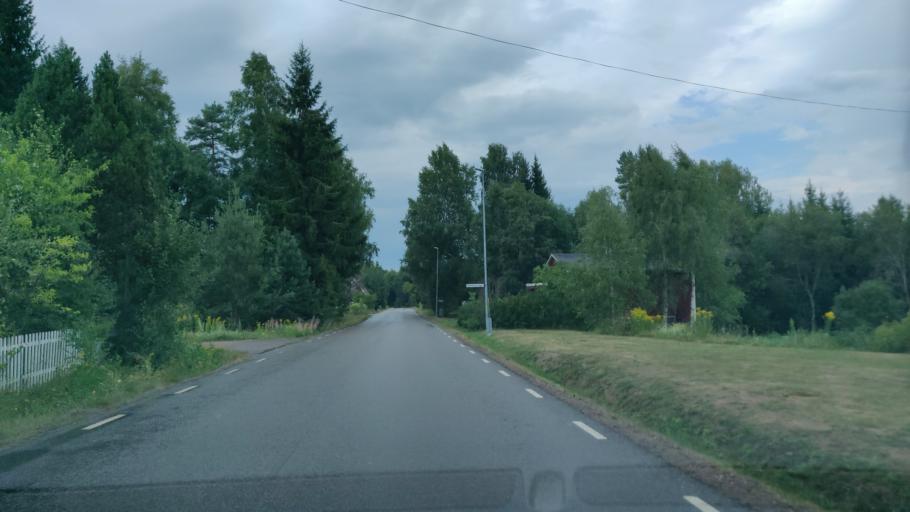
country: SE
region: Vaermland
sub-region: Munkfors Kommun
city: Munkfors
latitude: 59.8560
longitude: 13.5534
